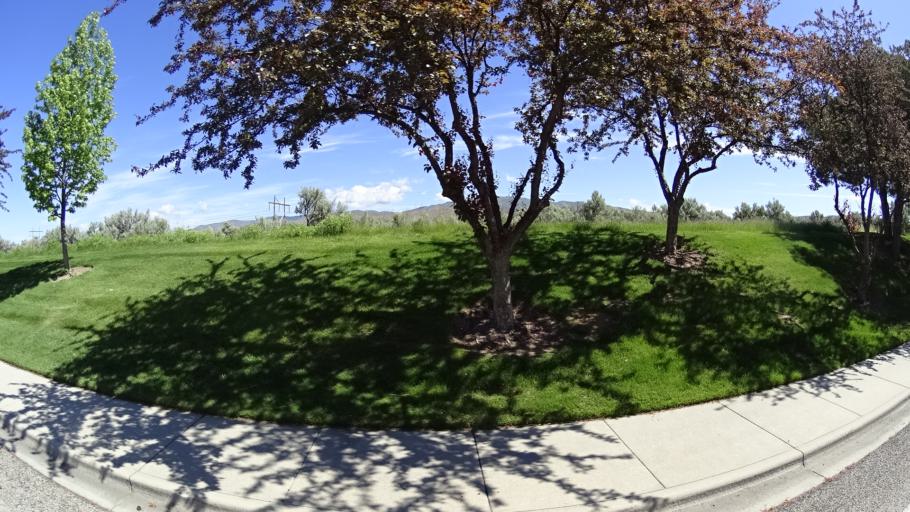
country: US
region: Idaho
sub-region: Ada County
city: Boise
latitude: 43.5487
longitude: -116.1201
